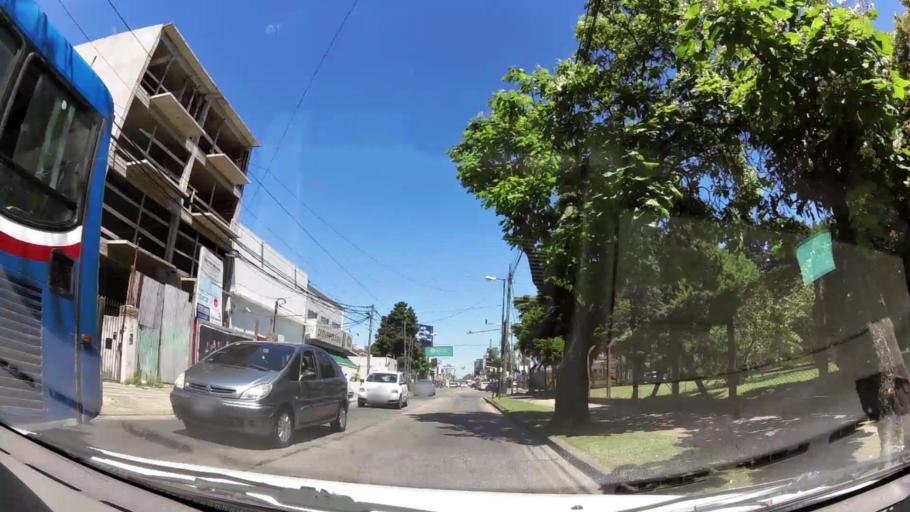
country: AR
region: Buenos Aires
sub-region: Partido de Vicente Lopez
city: Olivos
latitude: -34.5086
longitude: -58.5218
